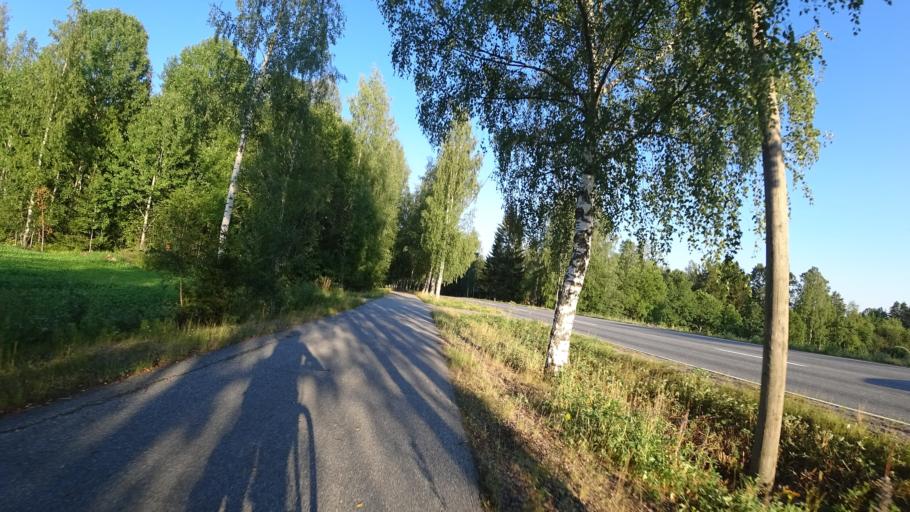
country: FI
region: Pirkanmaa
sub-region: Tampere
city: Nokia
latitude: 61.4716
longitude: 23.3846
